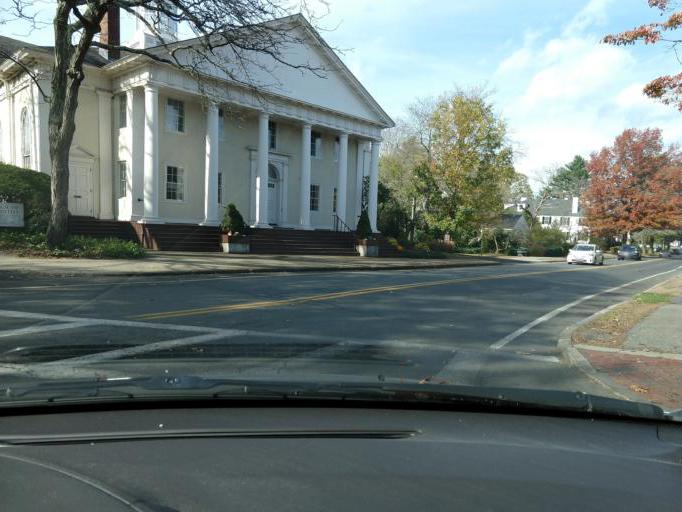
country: US
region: Massachusetts
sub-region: Middlesex County
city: Concord
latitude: 42.4614
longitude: -71.3496
